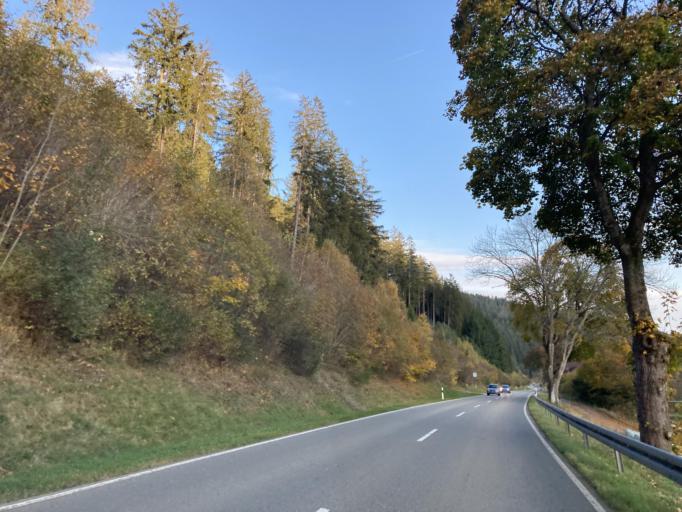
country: DE
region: Baden-Wuerttemberg
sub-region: Freiburg Region
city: Vohrenbach
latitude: 48.0072
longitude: 8.2917
